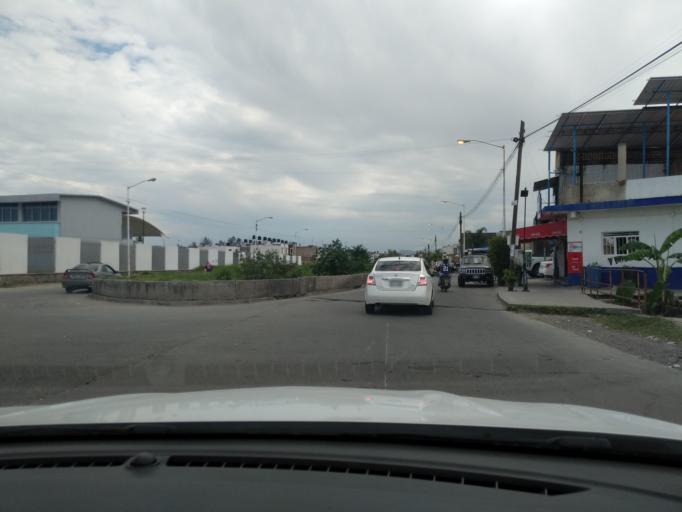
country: MX
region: Jalisco
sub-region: El Salto
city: Galaxia Bonito Jalisco
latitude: 20.5074
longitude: -103.1909
